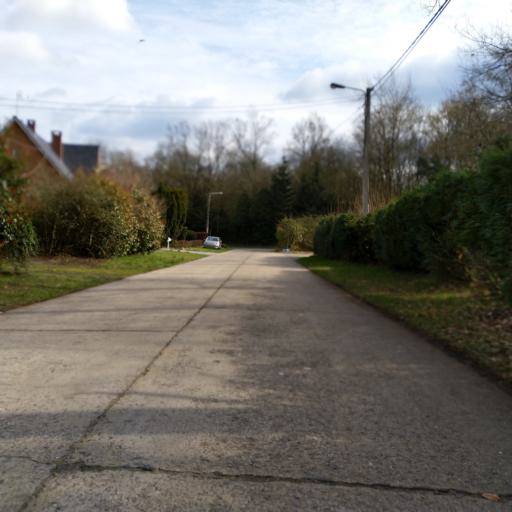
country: BE
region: Wallonia
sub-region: Province du Hainaut
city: Mons
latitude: 50.5074
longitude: 3.9928
